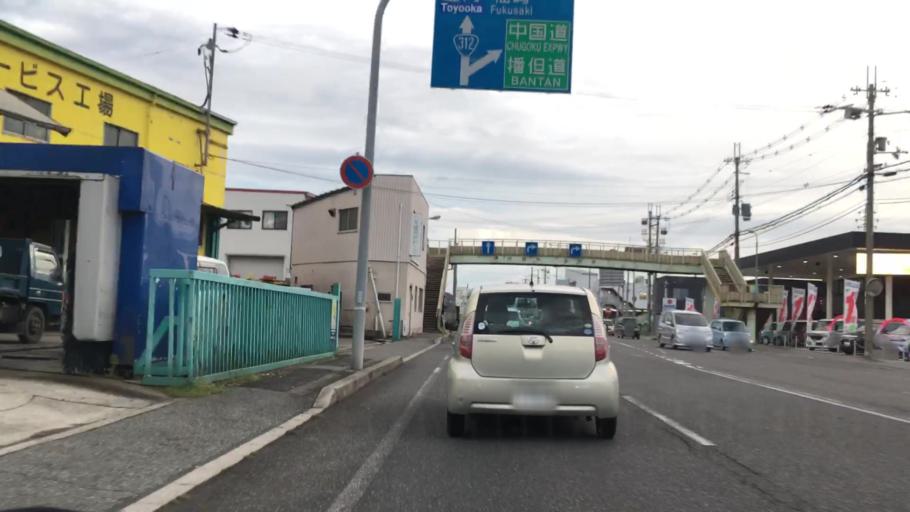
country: JP
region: Hyogo
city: Himeji
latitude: 34.8713
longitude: 134.7293
